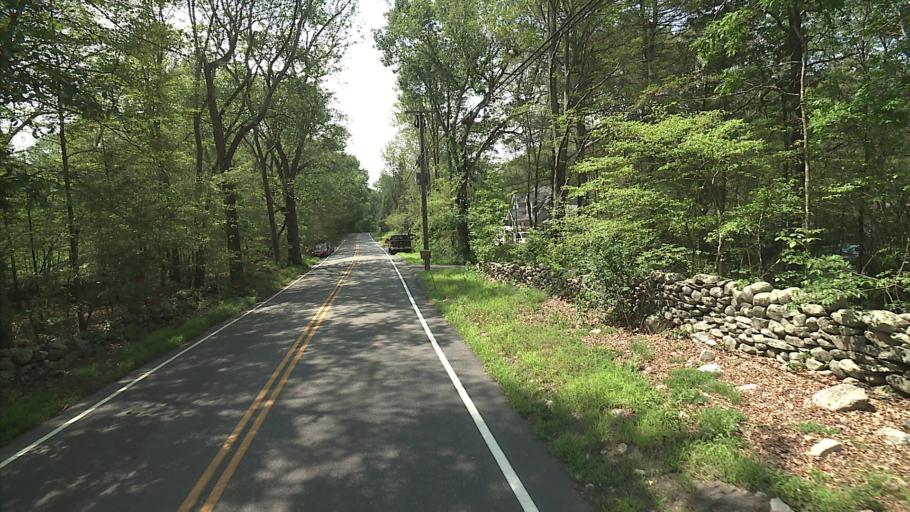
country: US
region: Connecticut
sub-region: Windham County
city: Danielson
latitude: 41.7668
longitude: -71.8463
